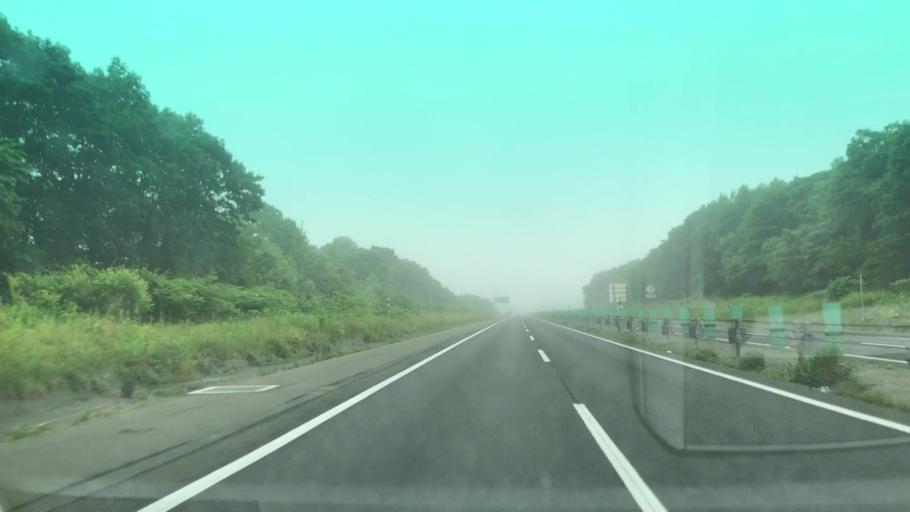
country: JP
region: Hokkaido
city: Chitose
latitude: 42.8229
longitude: 141.6164
